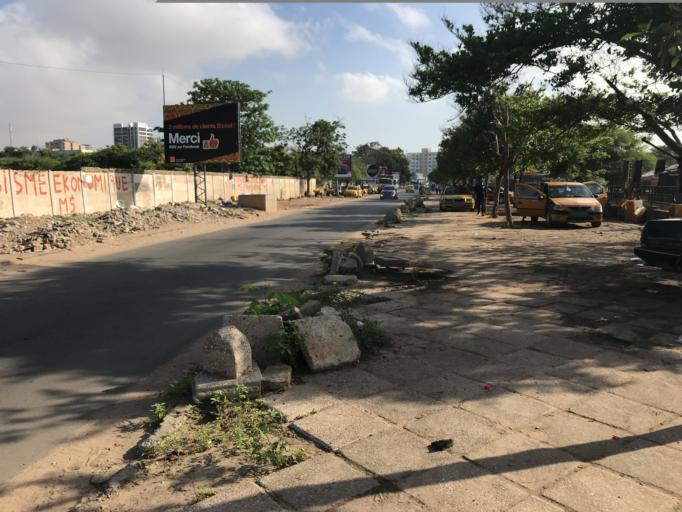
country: SN
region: Dakar
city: Dakar
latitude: 14.6870
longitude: -17.4605
